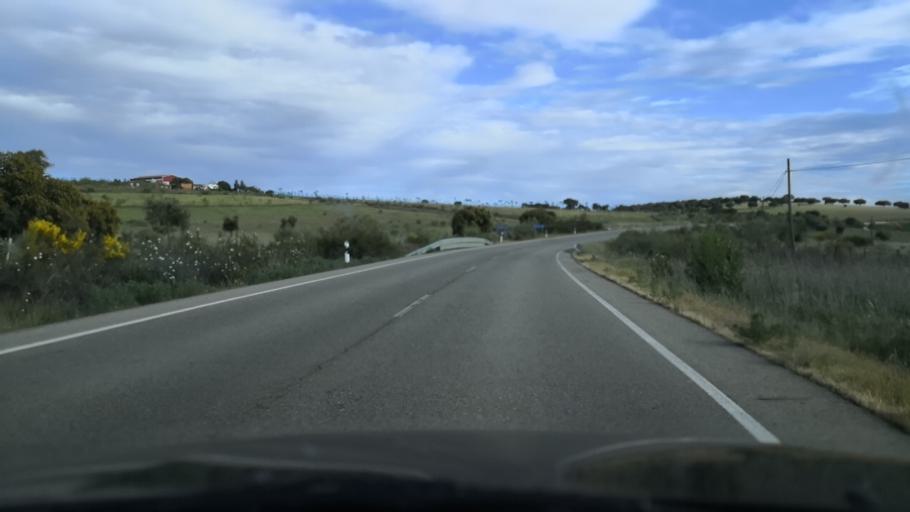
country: ES
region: Extremadura
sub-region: Provincia de Caceres
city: Perales del Puerto
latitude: 40.1171
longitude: -6.6707
